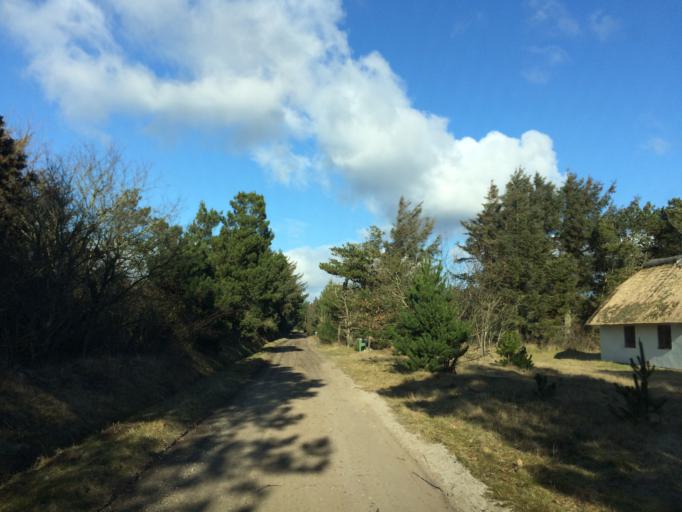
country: DK
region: Central Jutland
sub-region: Holstebro Kommune
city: Ulfborg
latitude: 56.2630
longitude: 8.1441
